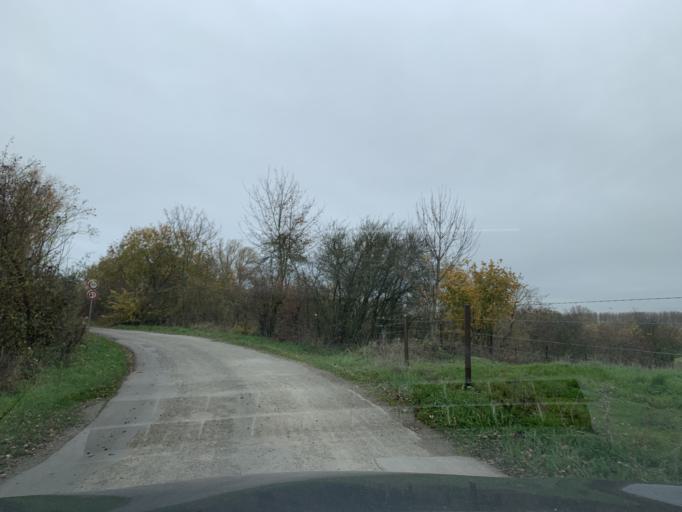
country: FR
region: Nord-Pas-de-Calais
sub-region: Departement du Pas-de-Calais
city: Oisy-le-Verger
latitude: 50.2488
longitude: 3.1005
